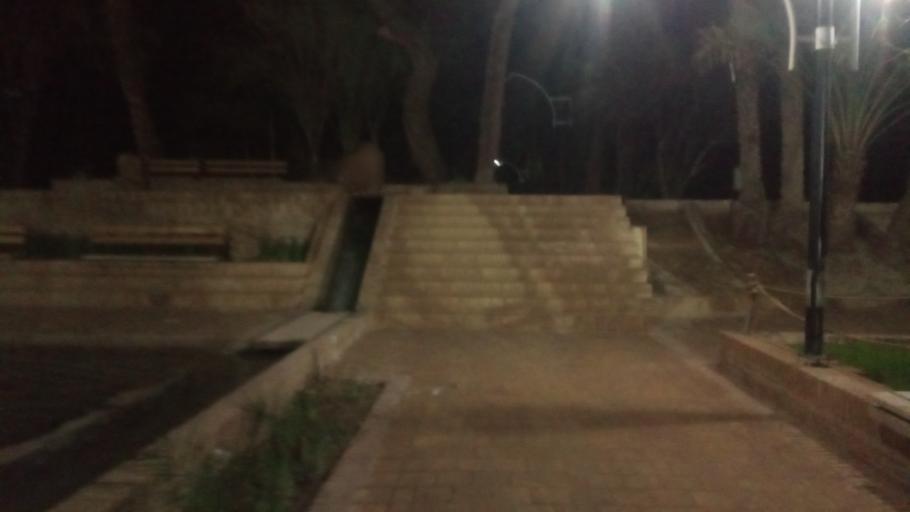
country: IR
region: Yazd
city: Tabas
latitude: 33.6014
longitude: 56.9439
